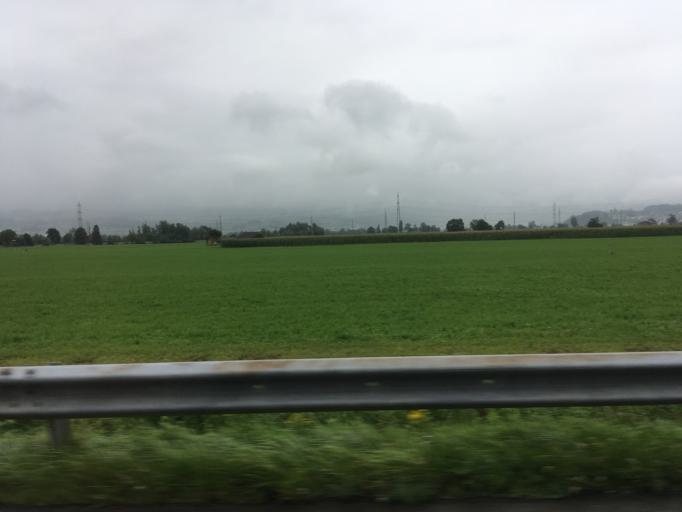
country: CH
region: Schwyz
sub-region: Bezirk March
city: Tuggen
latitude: 47.2007
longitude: 8.9683
